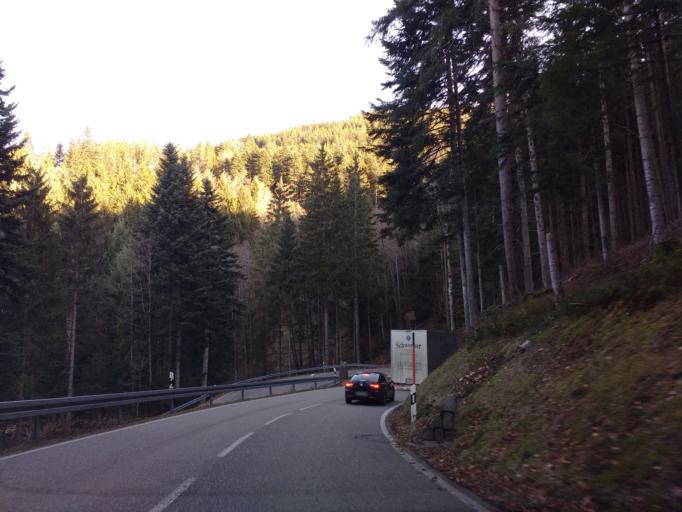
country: DE
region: Baden-Wuerttemberg
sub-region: Freiburg Region
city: Bad Peterstal-Griesbach
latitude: 48.4517
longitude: 8.2558
